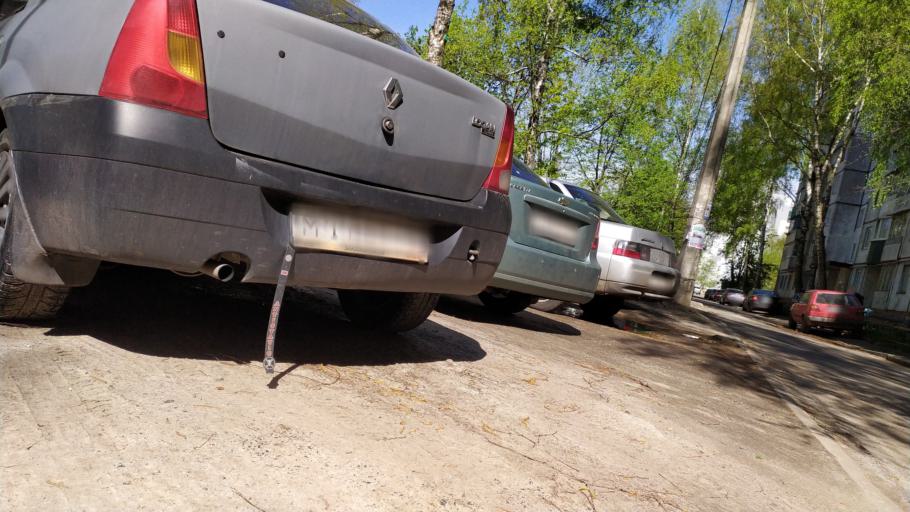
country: RU
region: Kursk
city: Kursk
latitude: 51.7391
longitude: 36.1366
